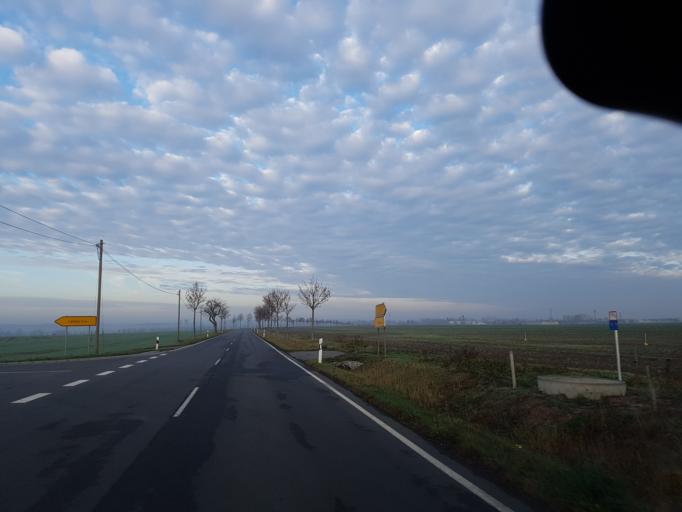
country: DE
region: Saxony-Anhalt
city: Zahna
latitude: 51.9041
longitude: 12.8172
